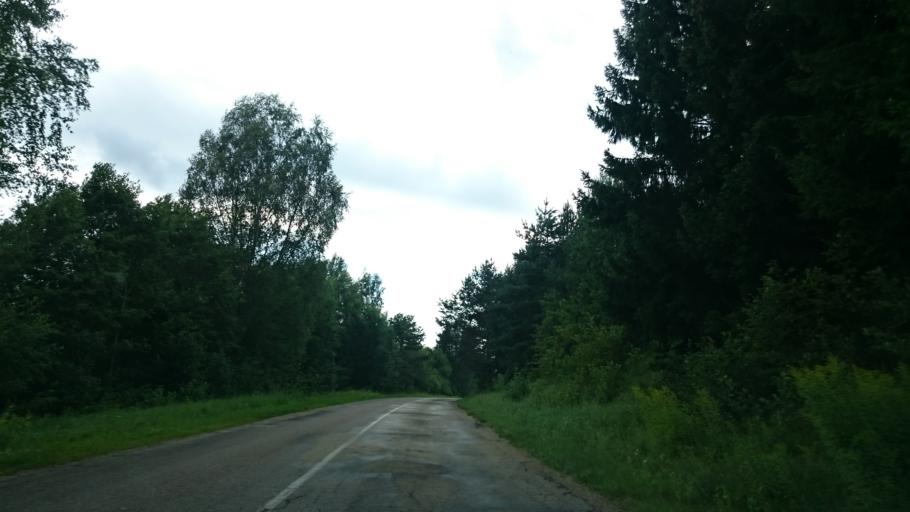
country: LV
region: Seja
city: Loja
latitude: 57.2166
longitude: 24.5769
